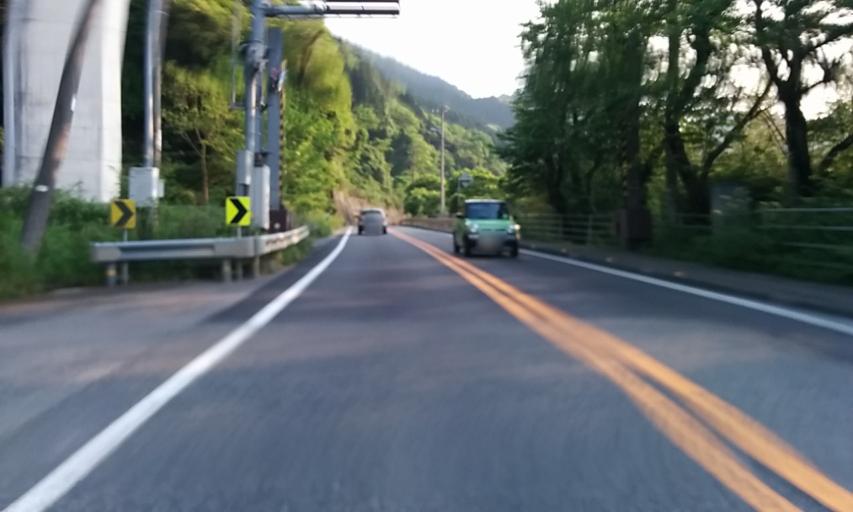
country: JP
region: Ehime
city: Saijo
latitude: 33.8541
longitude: 133.0118
